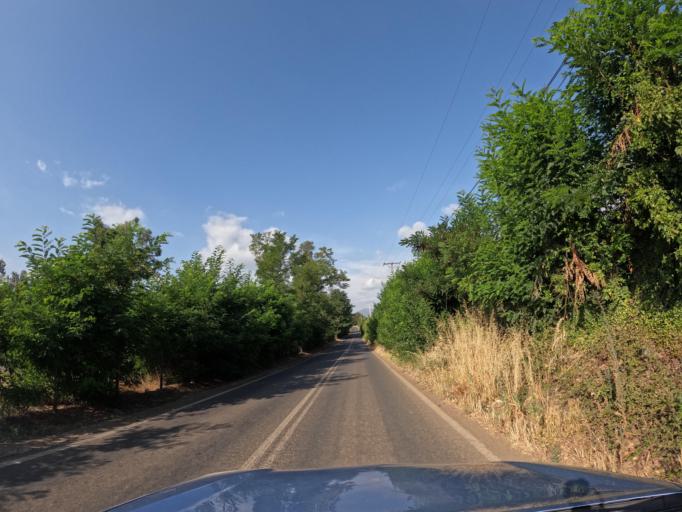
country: CL
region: Maule
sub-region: Provincia de Curico
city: Molina
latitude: -35.2726
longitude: -71.2500
